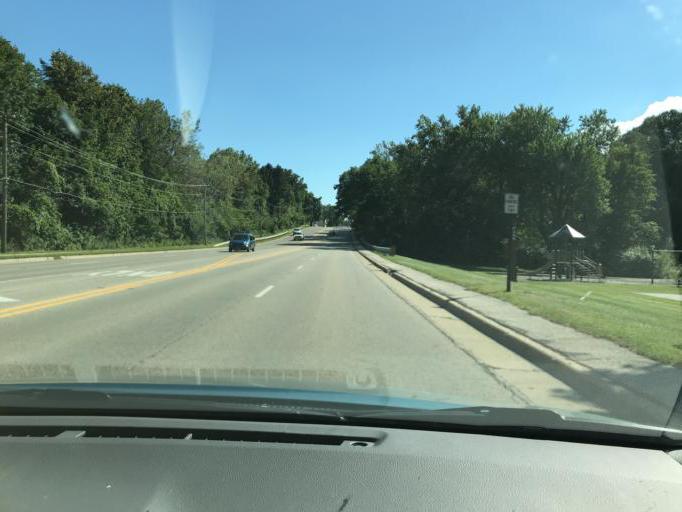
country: US
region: Illinois
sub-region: Lake County
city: Winthrop Harbor
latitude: 42.4875
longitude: -87.8221
